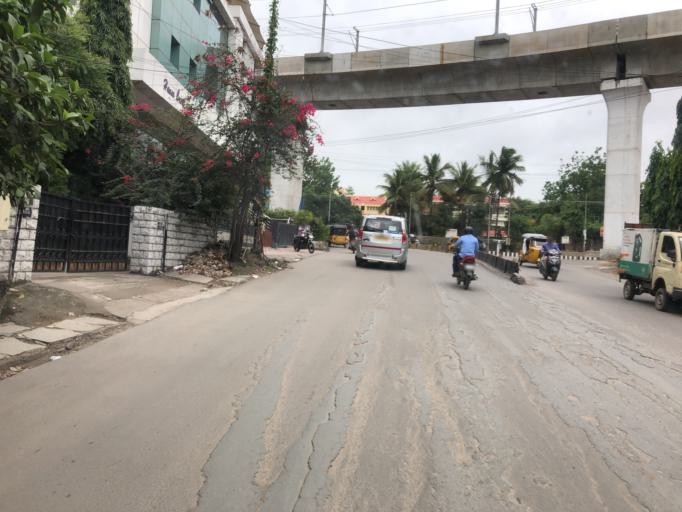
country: IN
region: Telangana
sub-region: Rangareddi
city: Kukatpalli
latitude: 17.4304
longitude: 78.4200
